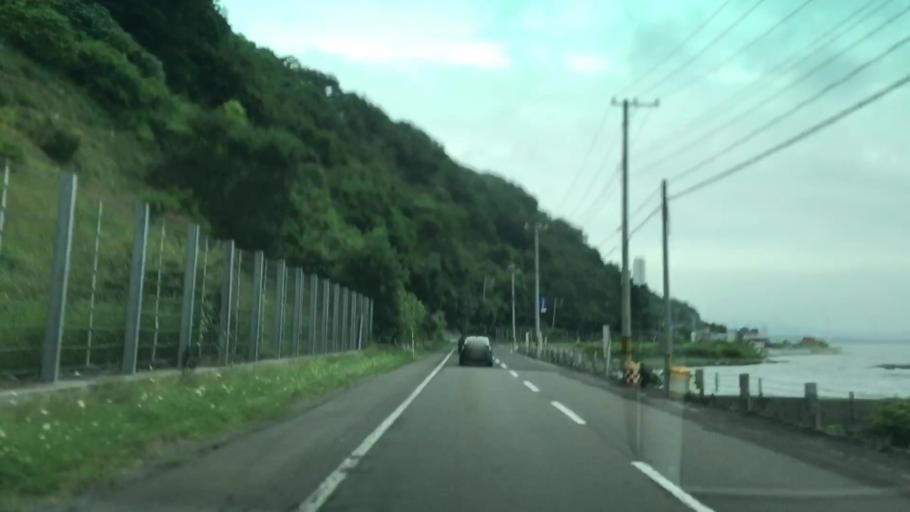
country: JP
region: Hokkaido
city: Iwanai
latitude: 42.7963
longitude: 140.3103
